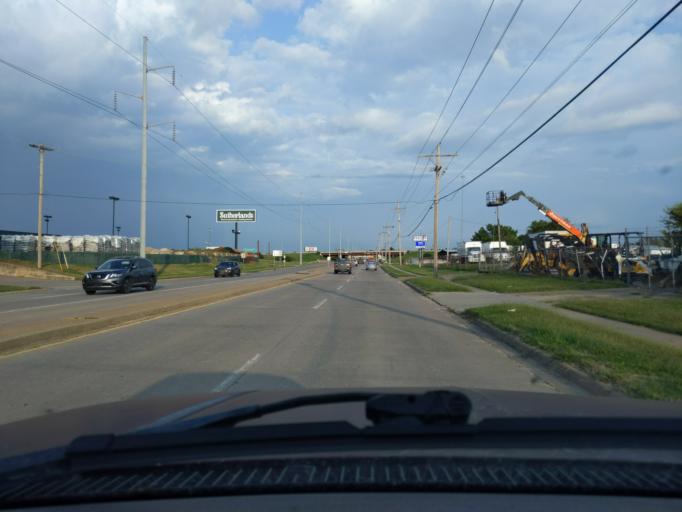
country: US
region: Oklahoma
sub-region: Tulsa County
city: Broken Arrow
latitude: 36.1334
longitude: -95.8729
